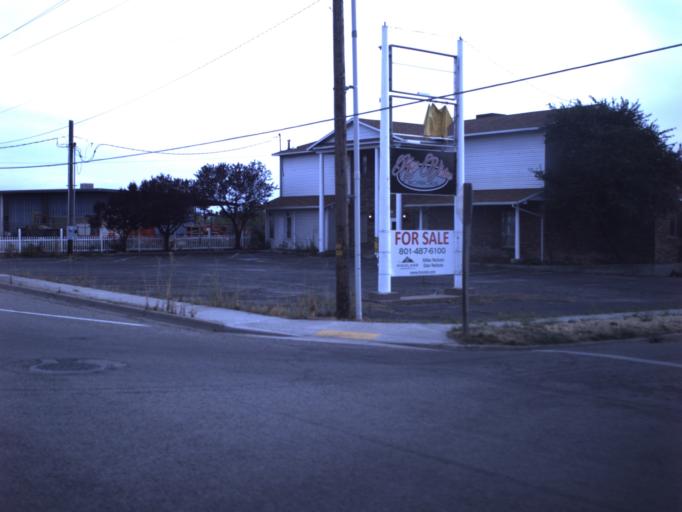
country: US
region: Utah
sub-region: Weber County
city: Marriott-Slaterville
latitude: 41.2741
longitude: -112.0282
